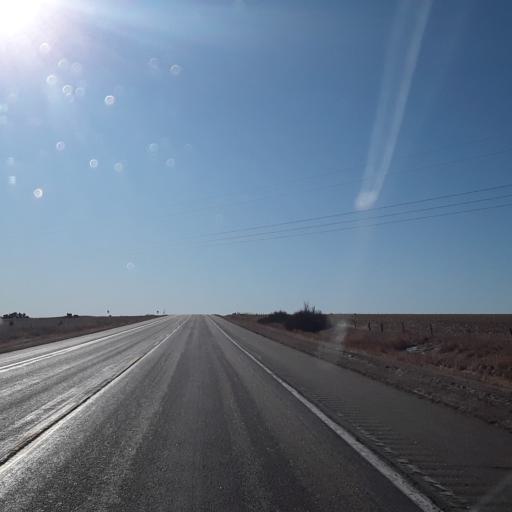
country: US
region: Nebraska
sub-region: Frontier County
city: Stockville
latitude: 40.5503
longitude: -100.6398
